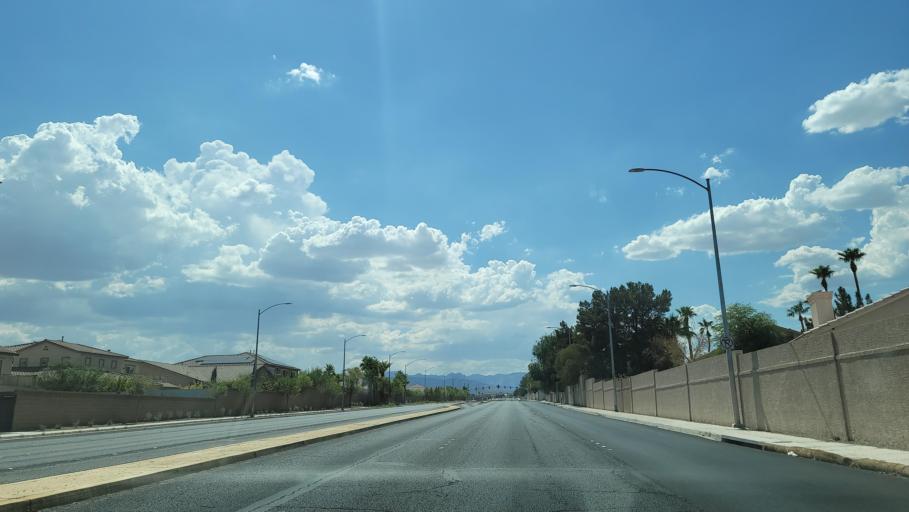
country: US
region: Nevada
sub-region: Clark County
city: Spring Valley
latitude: 36.1303
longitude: -115.2474
